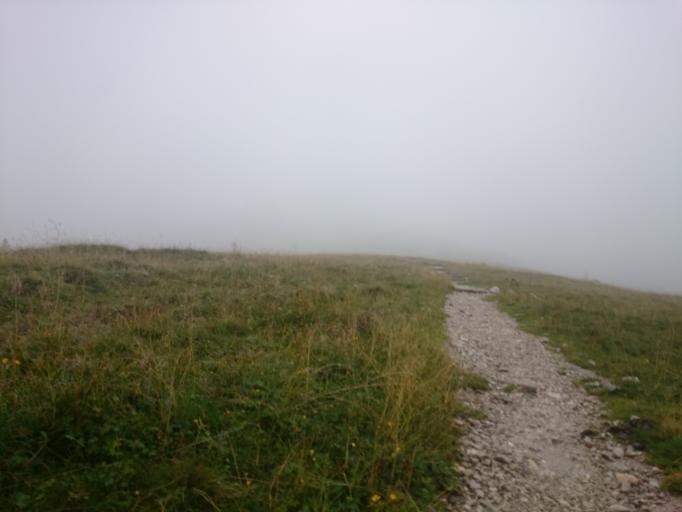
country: AT
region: Tyrol
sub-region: Politischer Bezirk Innsbruck Land
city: Absam
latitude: 47.4048
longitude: 11.4924
